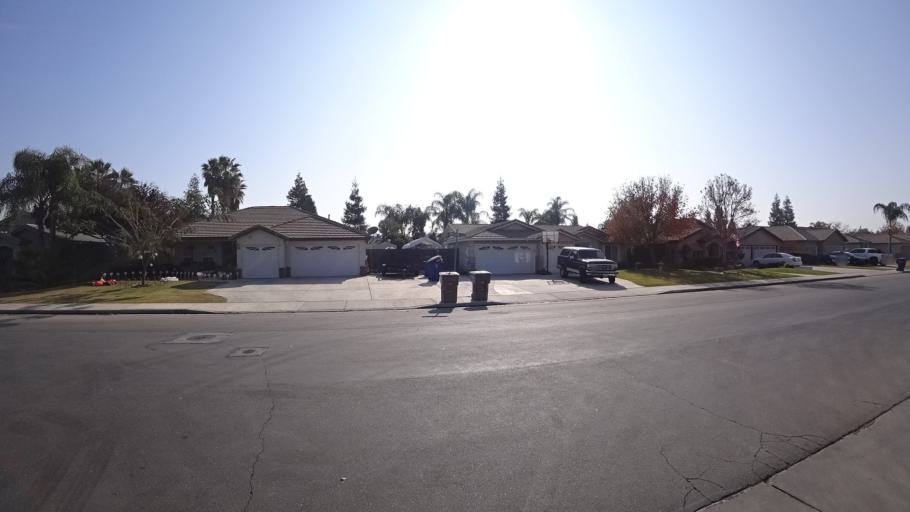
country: US
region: California
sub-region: Kern County
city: Greenacres
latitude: 35.4259
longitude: -119.1168
